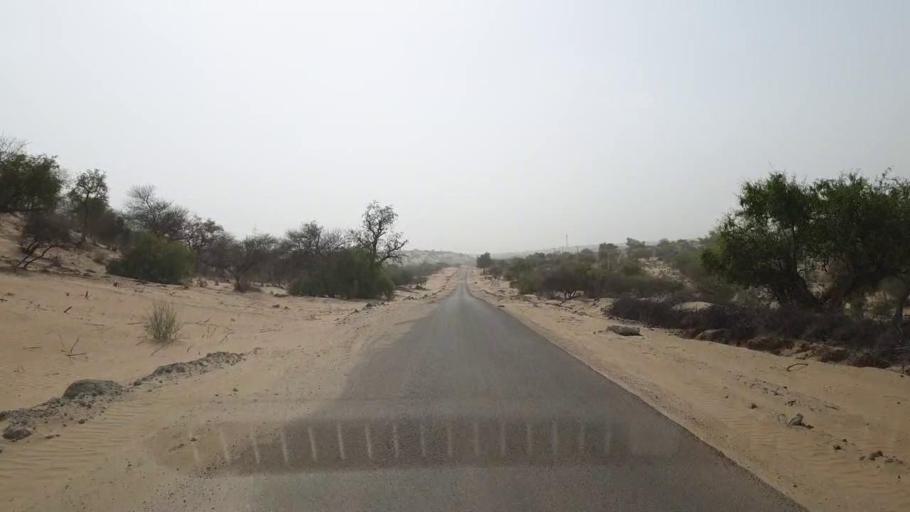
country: PK
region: Sindh
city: Mithi
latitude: 24.6208
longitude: 69.8780
